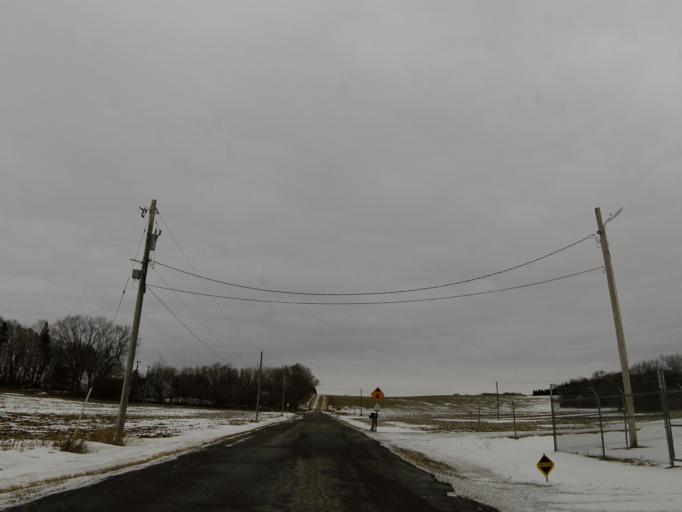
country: US
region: Minnesota
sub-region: Dakota County
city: Hastings
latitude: 44.8046
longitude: -92.8763
